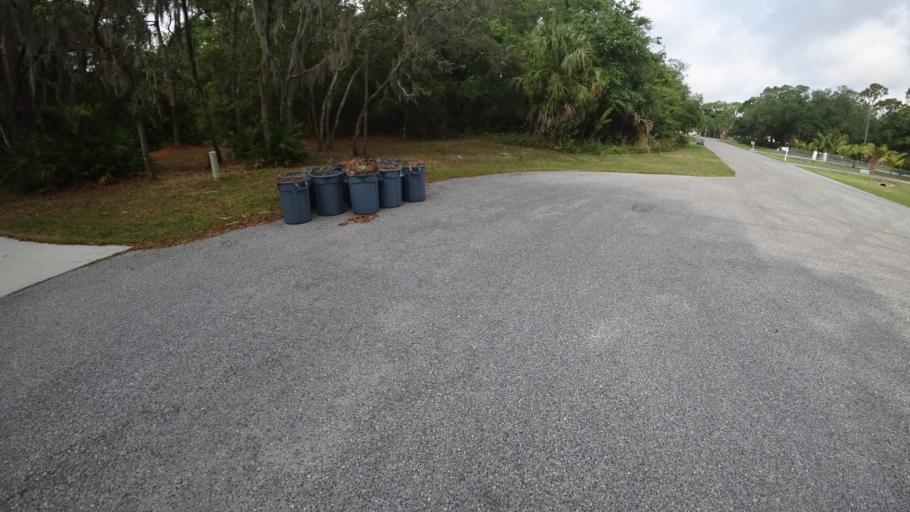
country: US
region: Florida
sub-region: Sarasota County
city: North Sarasota
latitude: 27.3988
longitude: -82.5121
